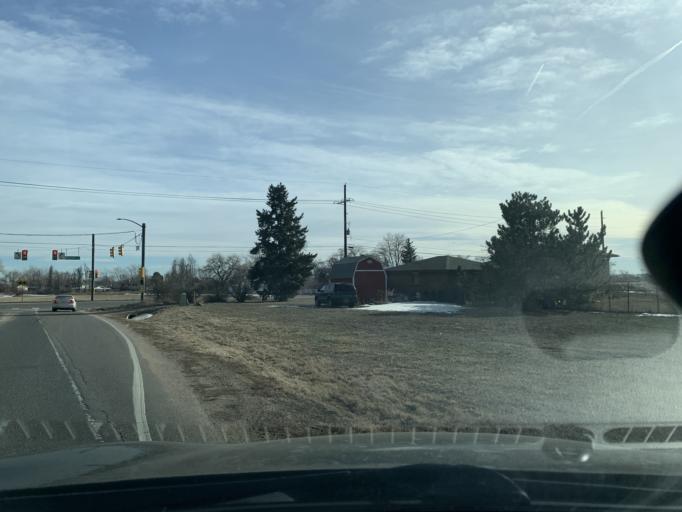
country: US
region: Colorado
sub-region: Jefferson County
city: Applewood
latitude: 39.7945
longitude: -105.1755
